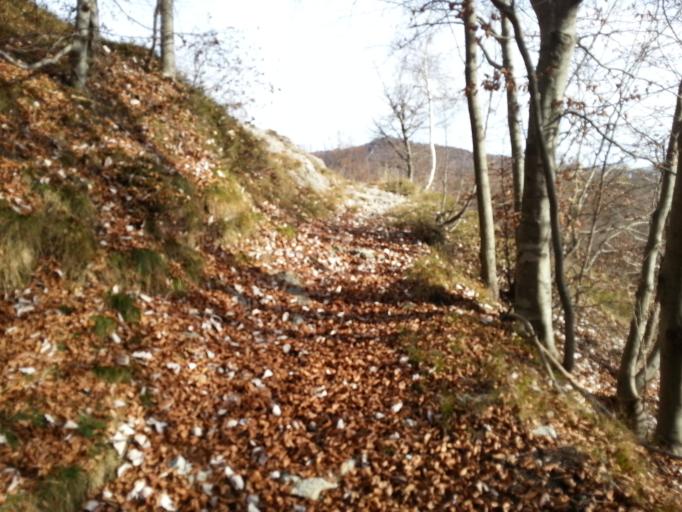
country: IT
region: Lombardy
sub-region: Provincia di Lecco
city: Morterone
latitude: 45.8878
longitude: 9.4785
